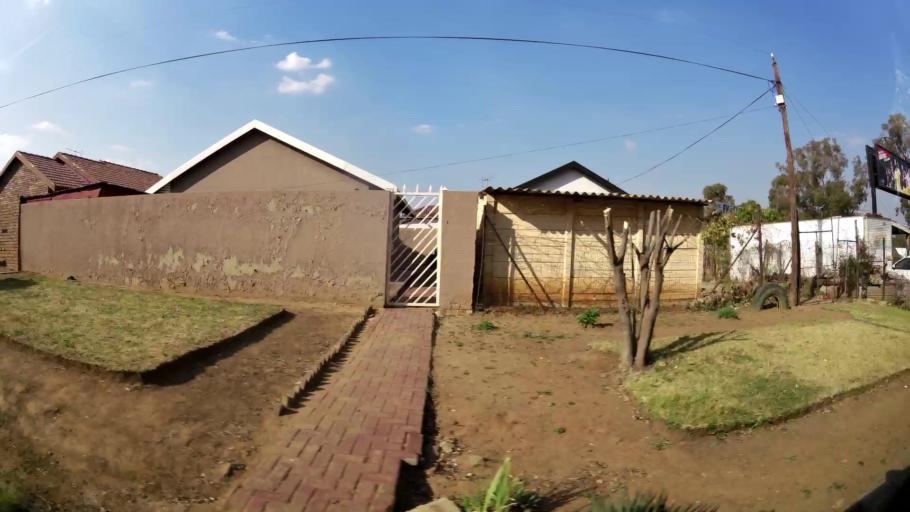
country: ZA
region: Gauteng
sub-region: Ekurhuleni Metropolitan Municipality
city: Brakpan
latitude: -26.1619
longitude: 28.4037
